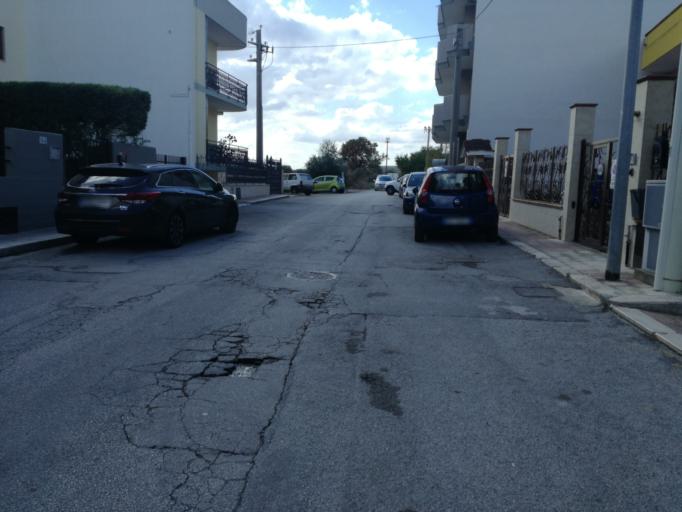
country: IT
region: Apulia
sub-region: Provincia di Bari
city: Triggiano
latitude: 41.0664
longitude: 16.9355
